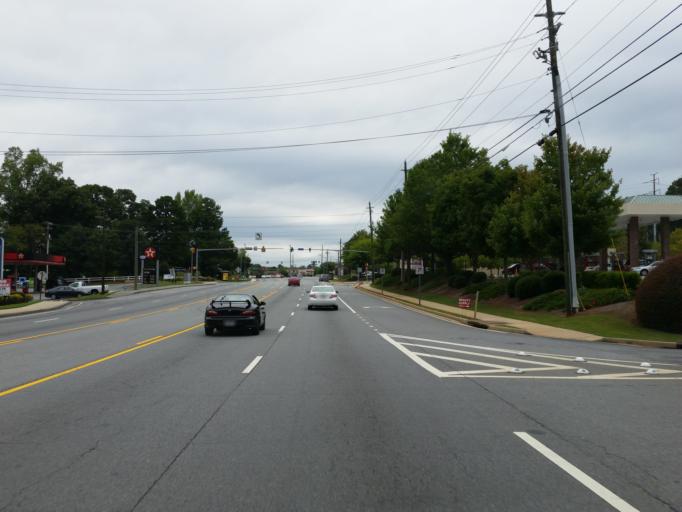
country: US
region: Georgia
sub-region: Cobb County
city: Fair Oaks
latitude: 33.9084
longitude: -84.6009
